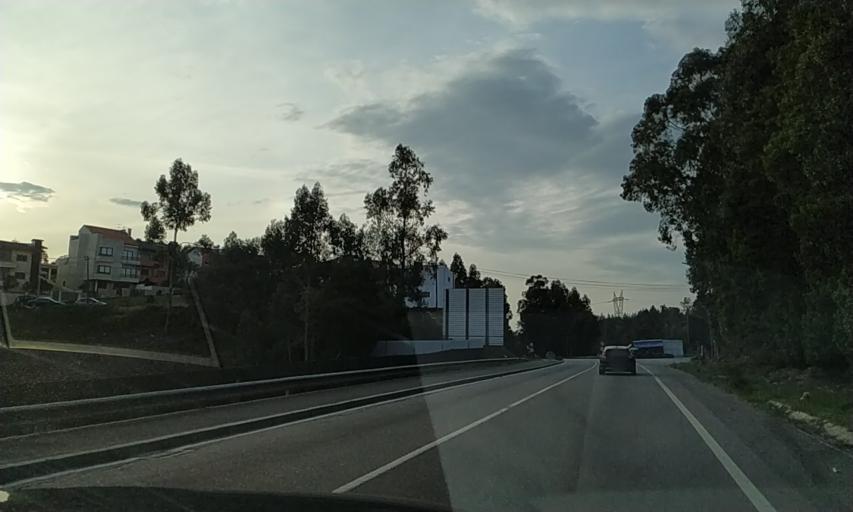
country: PT
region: Porto
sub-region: Valongo
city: Valongo
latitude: 41.1956
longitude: -8.5193
